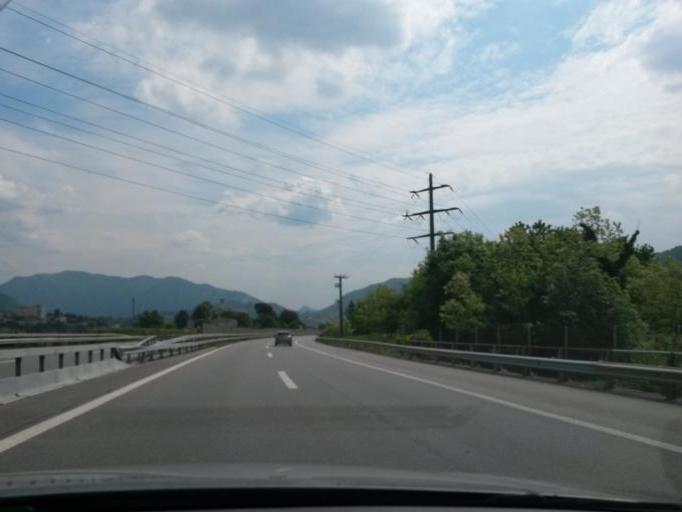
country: CH
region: Ticino
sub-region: Mendrisio District
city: Novazzano
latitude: 45.8472
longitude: 8.9916
